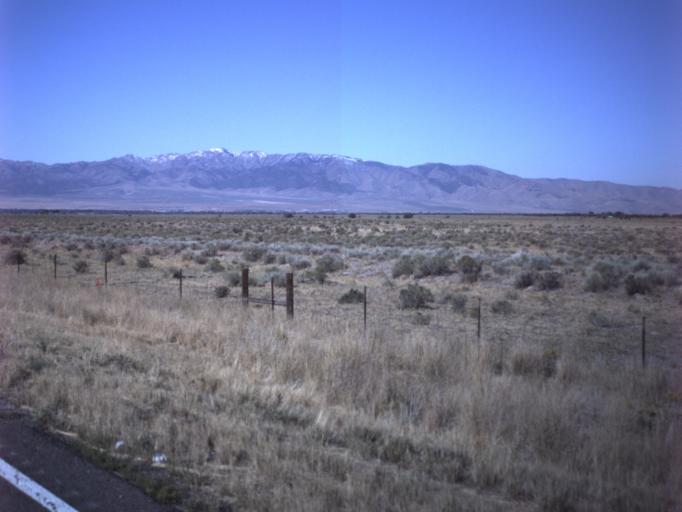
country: US
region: Utah
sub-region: Tooele County
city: Erda
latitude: 40.6147
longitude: -112.3706
